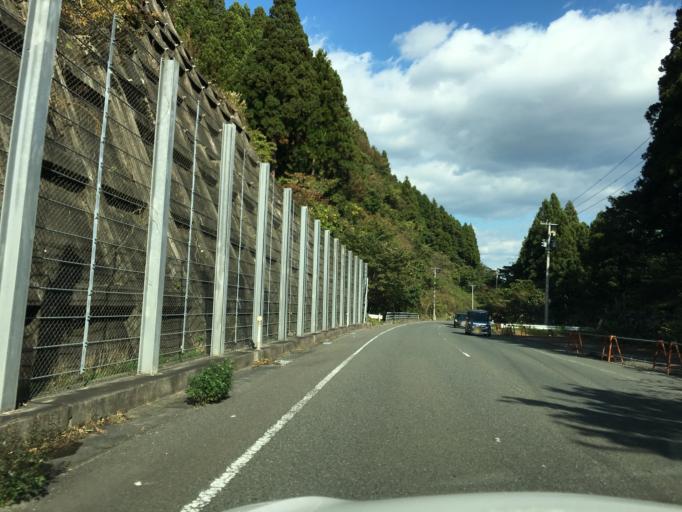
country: JP
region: Fukushima
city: Namie
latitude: 37.3590
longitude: 140.9499
